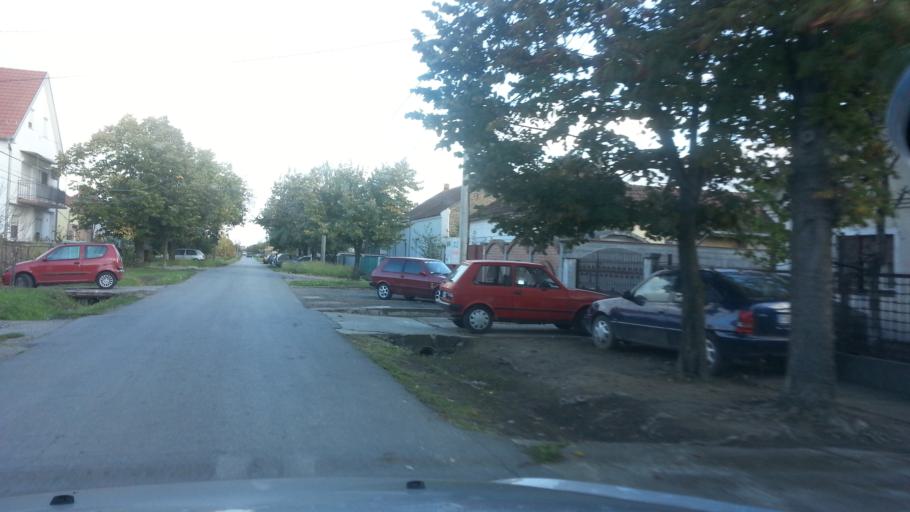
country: RS
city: Novi Banovci
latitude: 44.9079
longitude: 20.2657
